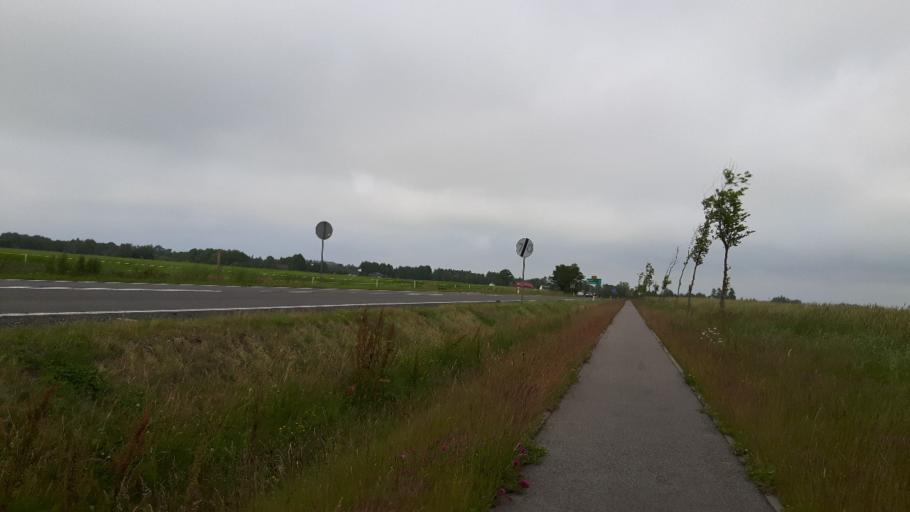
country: PL
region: West Pomeranian Voivodeship
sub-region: Powiat koszalinski
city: Sianow
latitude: 54.3183
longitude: 16.3043
